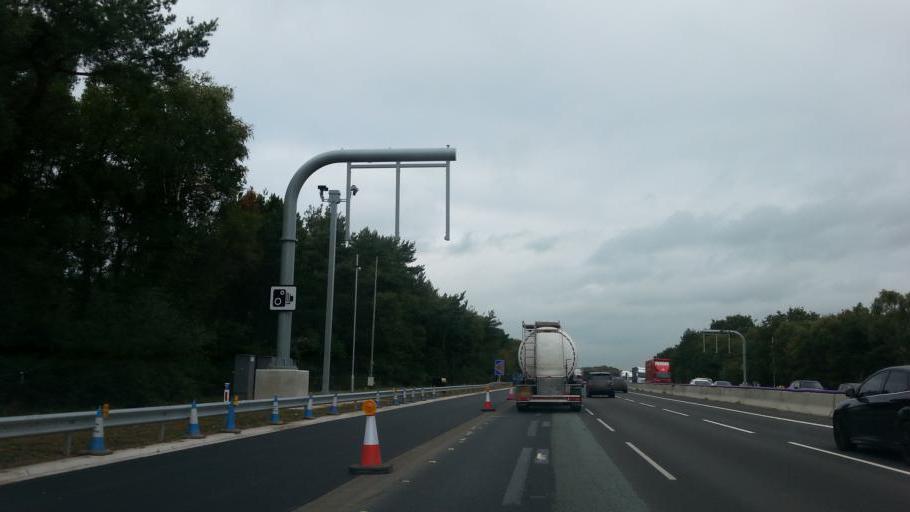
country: GB
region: England
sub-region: Cheshire East
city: Peover Superior
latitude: 53.2360
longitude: -2.3999
